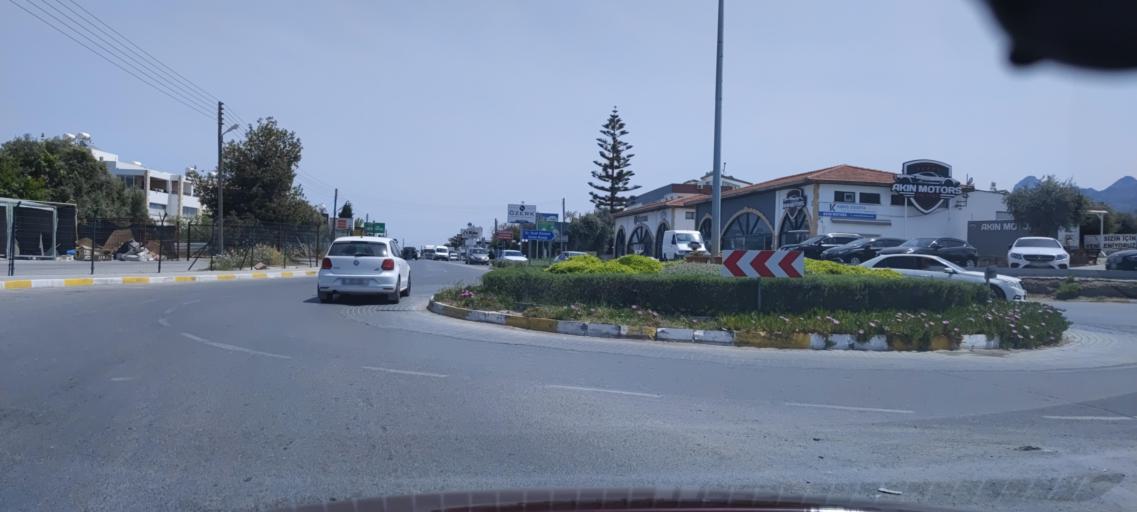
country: CY
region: Keryneia
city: Kyrenia
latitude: 35.3318
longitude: 33.3387
